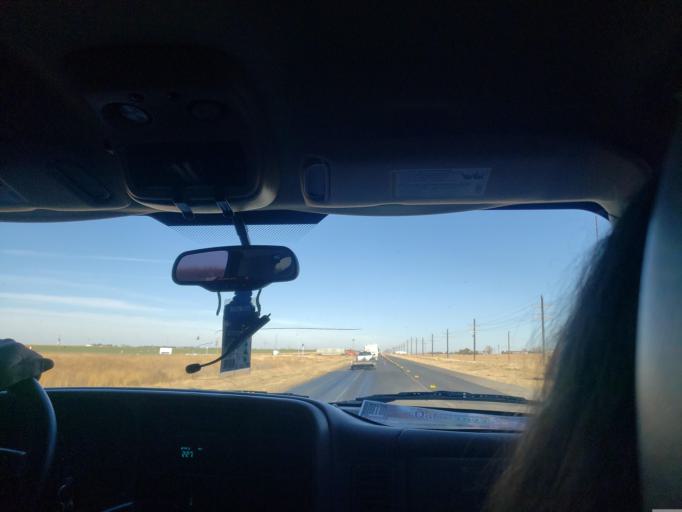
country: US
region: Texas
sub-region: Dallam County
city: Dalhart
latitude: 36.0197
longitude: -102.5821
